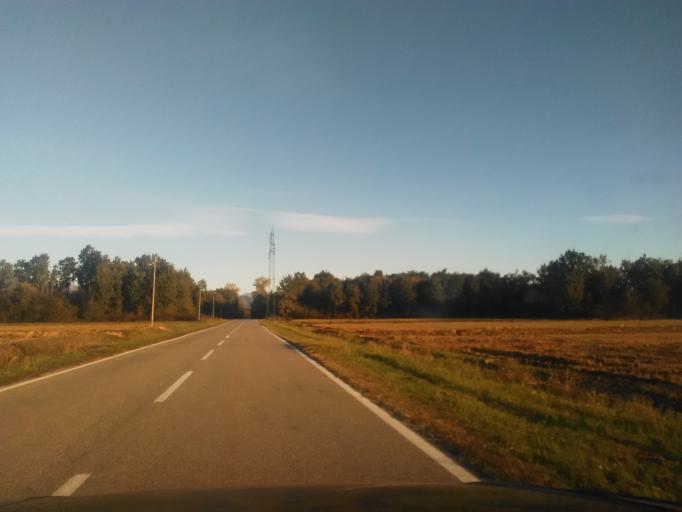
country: IT
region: Piedmont
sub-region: Provincia di Vercelli
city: Rovasenda
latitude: 45.5659
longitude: 8.2966
